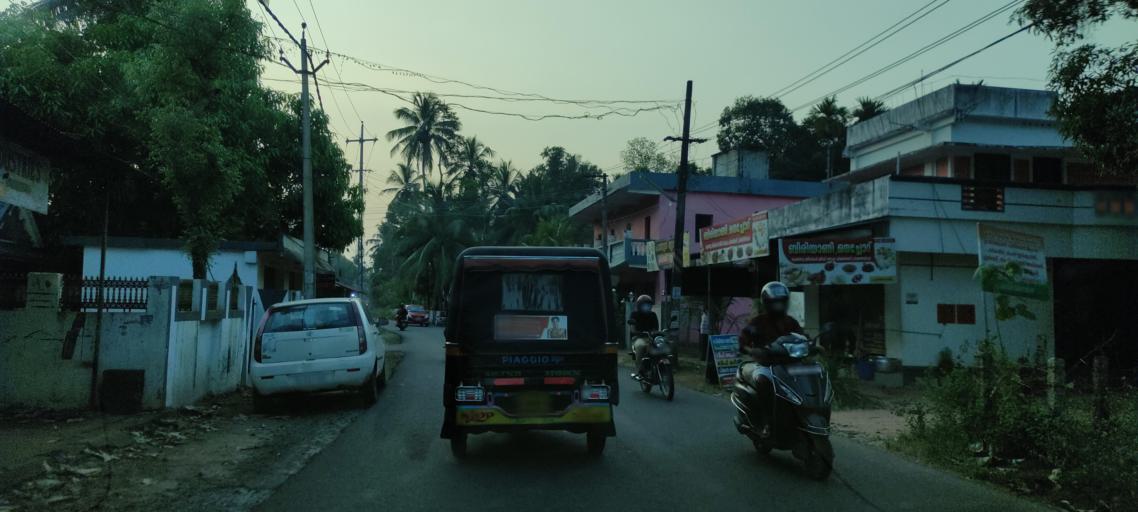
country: IN
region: Kerala
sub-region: Alappuzha
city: Kayankulam
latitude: 9.1377
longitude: 76.5153
